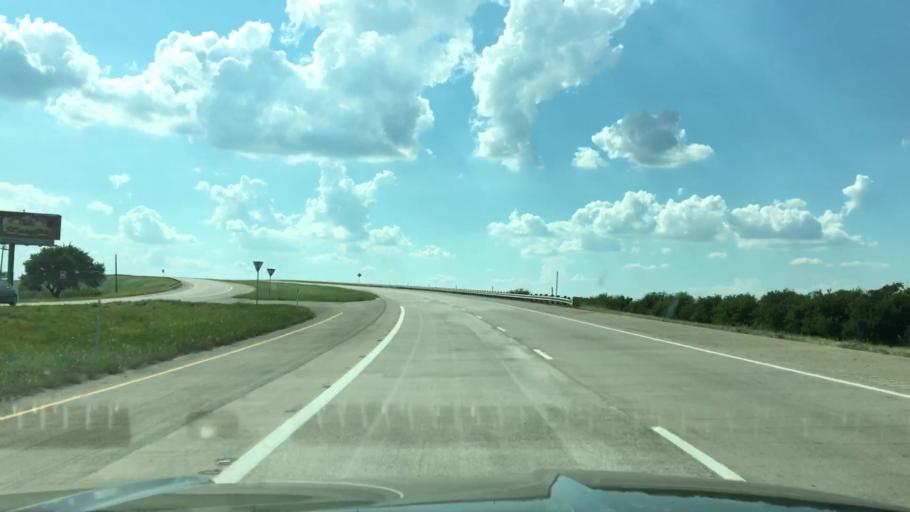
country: US
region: Texas
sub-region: Wise County
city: Rhome
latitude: 33.0462
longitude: -97.4565
